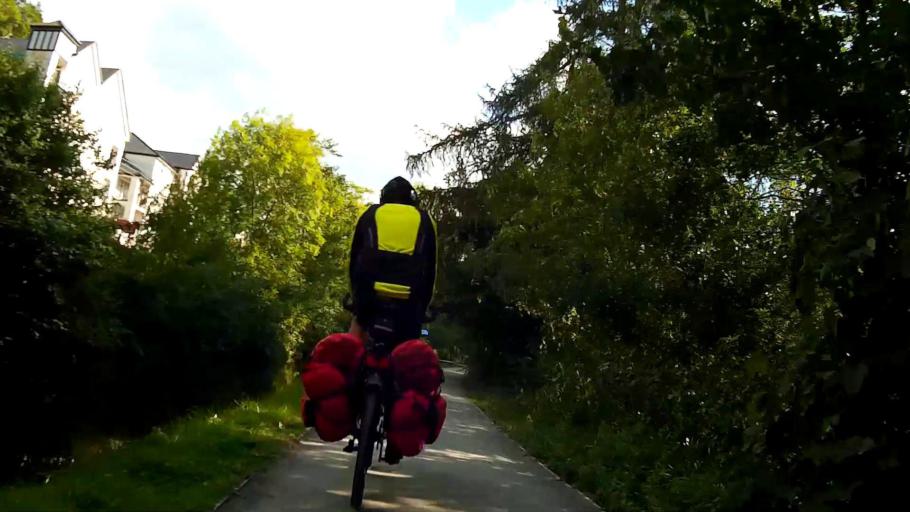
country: GB
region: Wales
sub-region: Denbighshire
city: Llangollen
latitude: 52.9726
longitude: -3.1722
